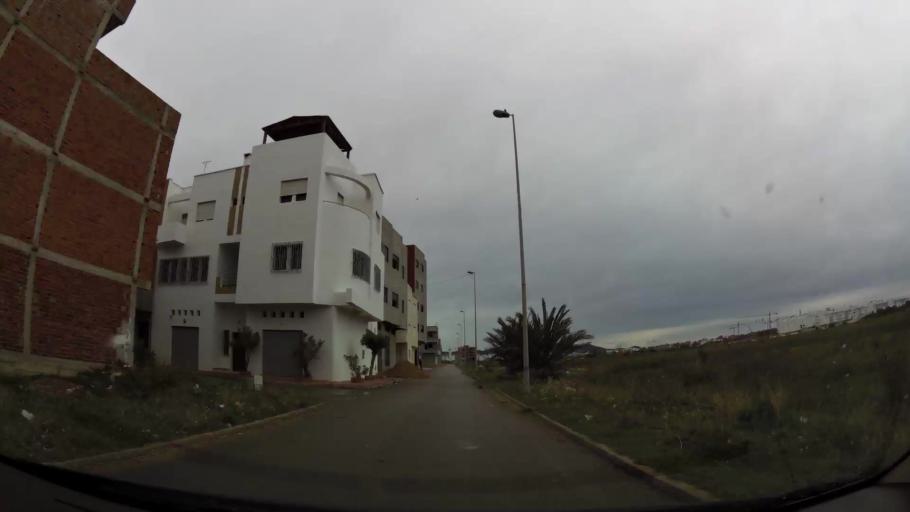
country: MA
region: Tanger-Tetouan
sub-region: Tetouan
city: Martil
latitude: 35.6149
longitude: -5.2980
